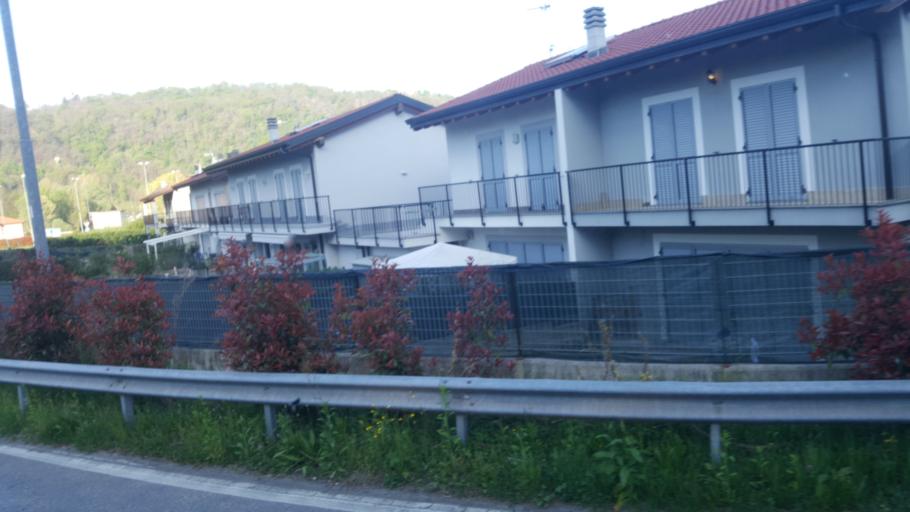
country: IT
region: Lombardy
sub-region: Provincia di Varese
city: Luino
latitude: 45.9828
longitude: 8.7491
